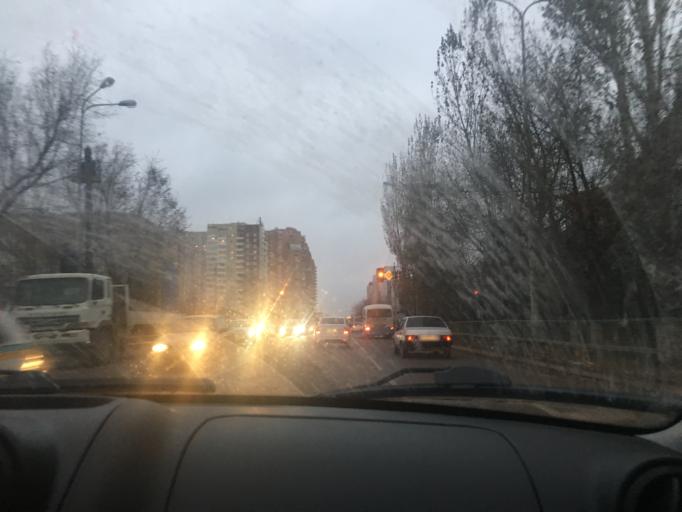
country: KZ
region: Astana Qalasy
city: Astana
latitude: 51.1606
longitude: 71.4419
